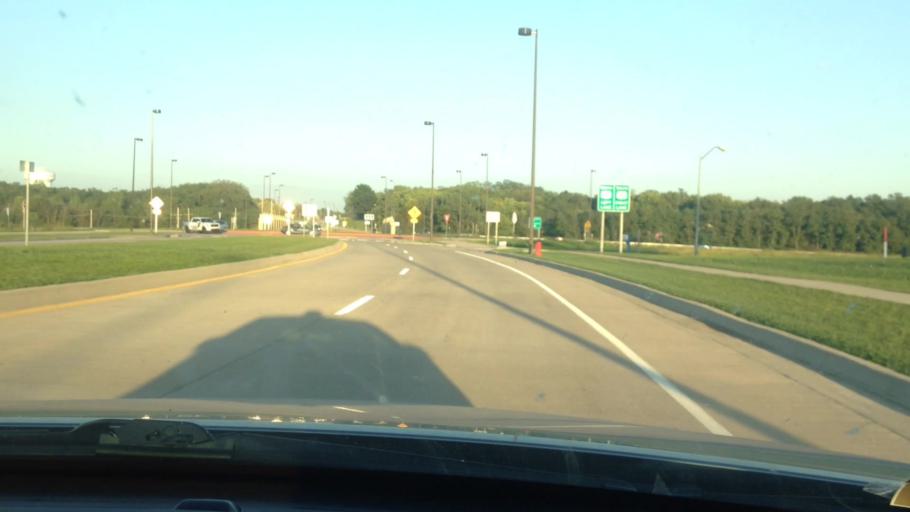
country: US
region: Missouri
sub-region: Clay County
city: Gladstone
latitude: 39.2891
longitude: -94.5879
